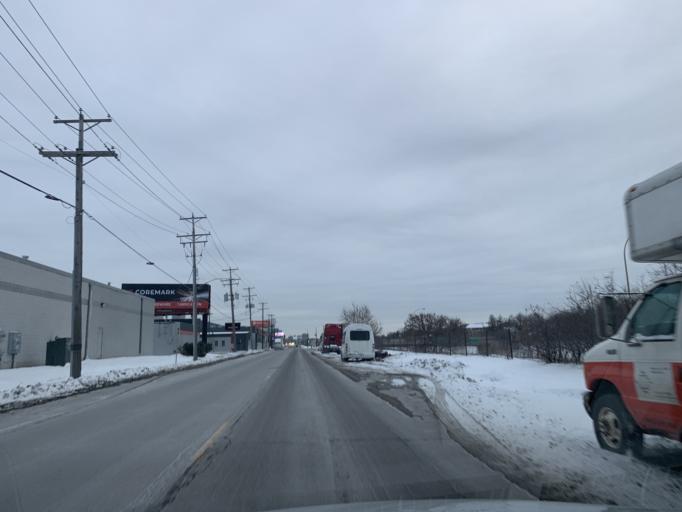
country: US
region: Minnesota
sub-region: Hennepin County
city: Minneapolis
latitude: 45.0083
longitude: -93.2819
